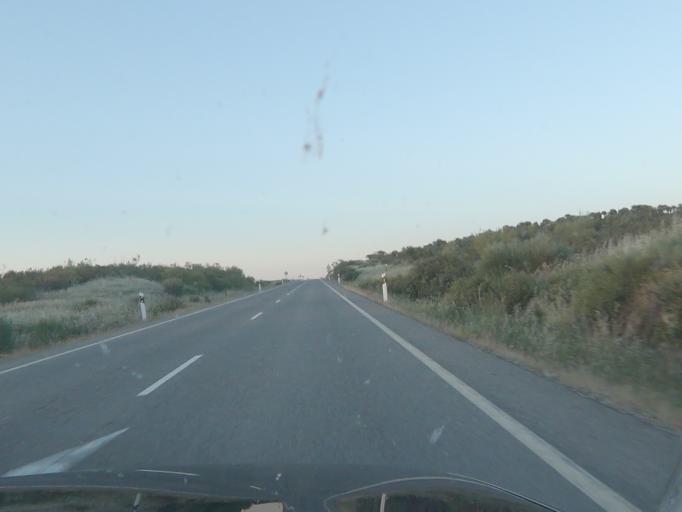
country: ES
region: Extremadura
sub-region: Provincia de Caceres
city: Salorino
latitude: 39.6043
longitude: -6.9746
